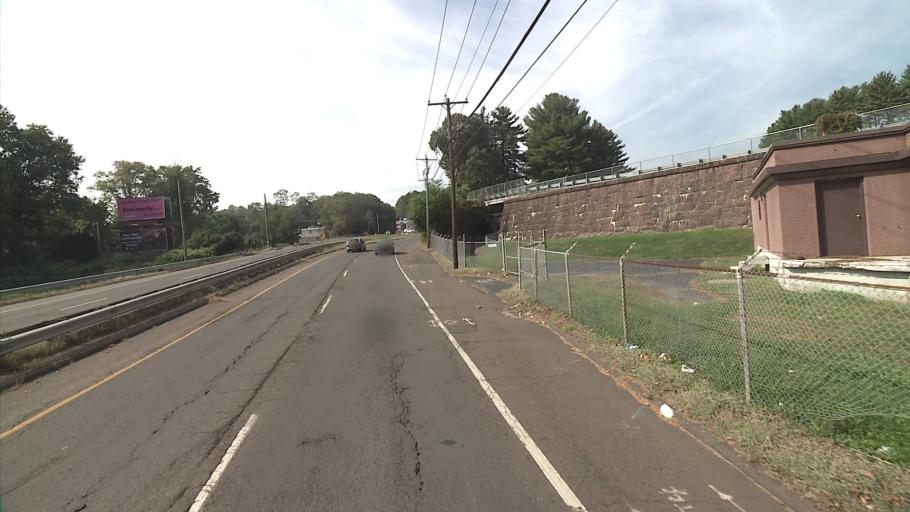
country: US
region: Connecticut
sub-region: New Haven County
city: West Haven
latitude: 41.3055
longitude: -72.9730
